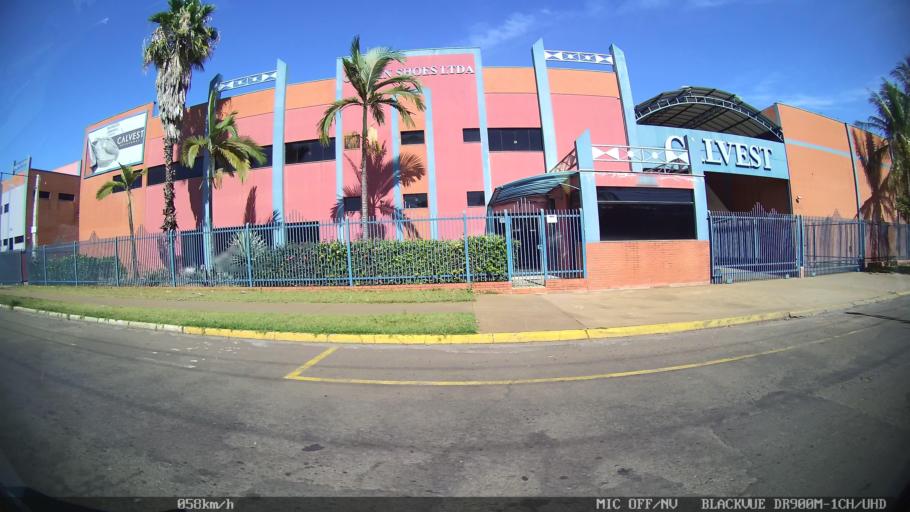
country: BR
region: Sao Paulo
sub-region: Franca
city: Franca
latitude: -20.5529
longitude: -47.4410
